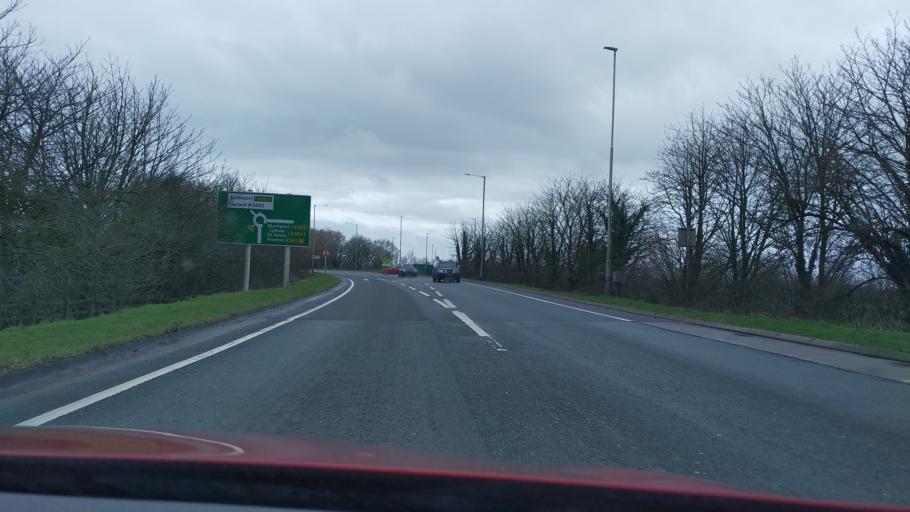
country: GB
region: England
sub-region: Lancashire
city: Leyland
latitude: 53.7155
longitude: -2.7115
